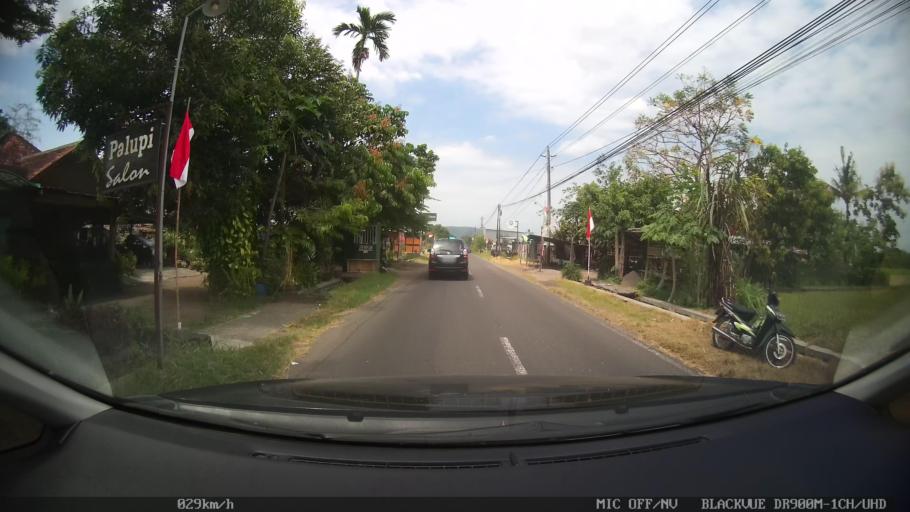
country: ID
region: Daerah Istimewa Yogyakarta
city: Depok
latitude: -7.8174
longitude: 110.4428
